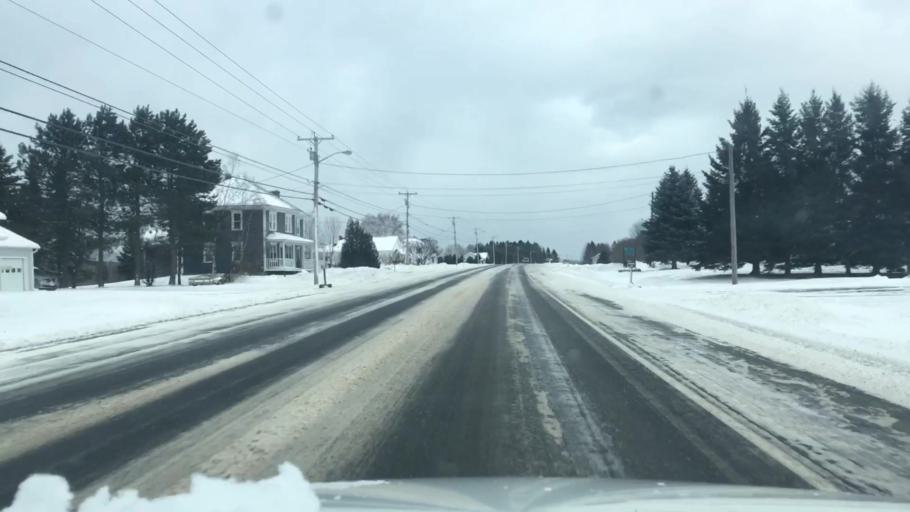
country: US
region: Maine
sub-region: Aroostook County
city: Madawaska
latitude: 47.3442
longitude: -68.2449
